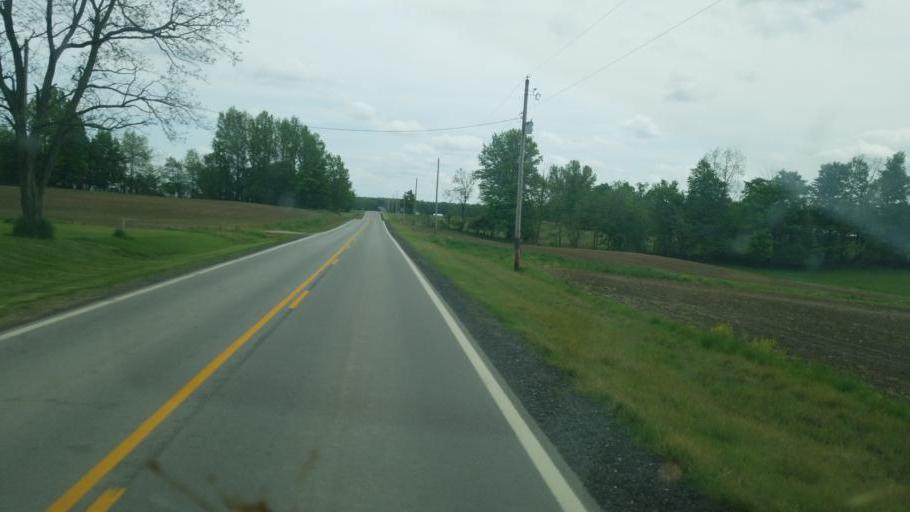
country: US
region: Ohio
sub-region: Crawford County
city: Bucyrus
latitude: 40.9297
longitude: -83.0520
